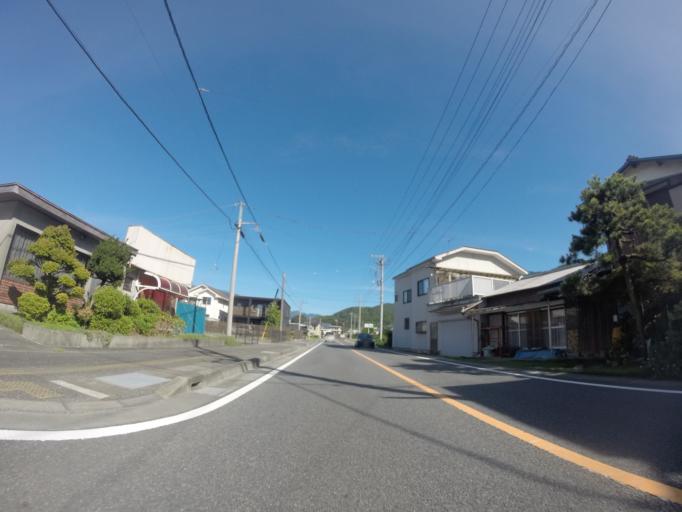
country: JP
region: Shizuoka
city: Fujinomiya
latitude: 35.2779
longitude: 138.4667
